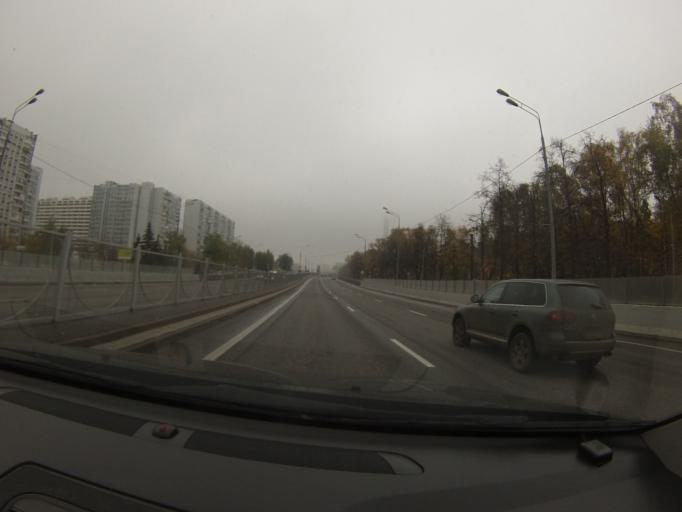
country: RU
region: Moskovskaya
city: Bol'shaya Setun'
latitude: 55.7496
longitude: 37.4123
